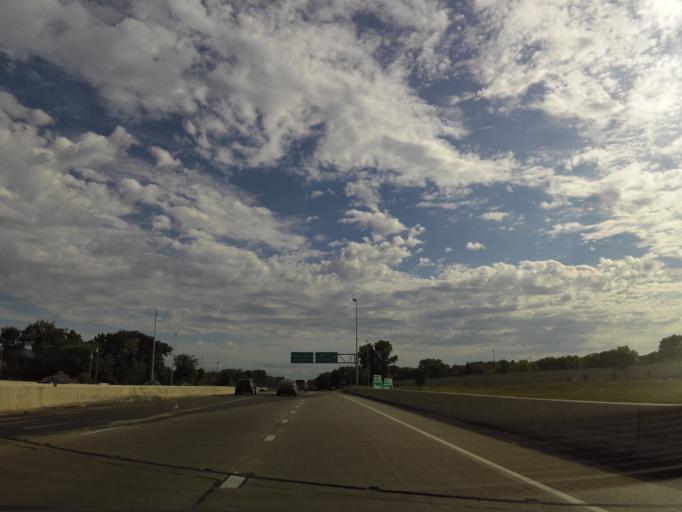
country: US
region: Minnesota
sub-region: Hennepin County
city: Osseo
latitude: 45.0837
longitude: -93.4024
